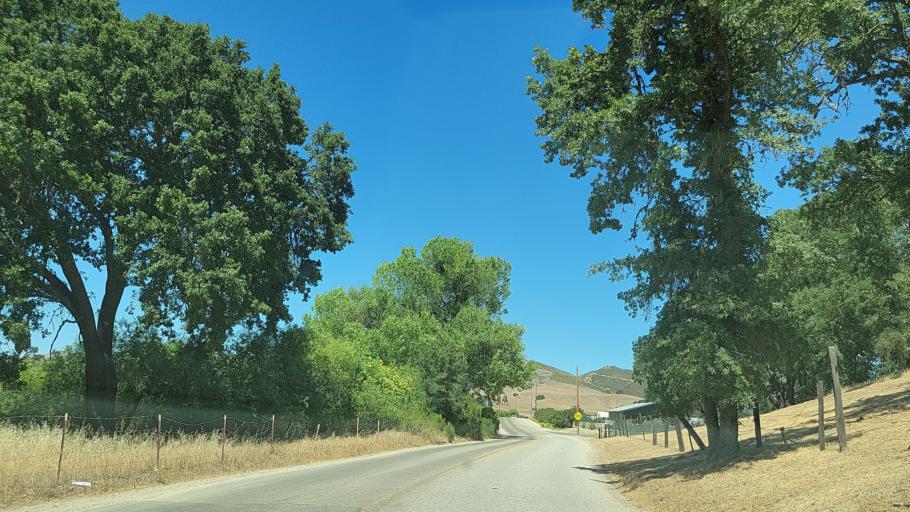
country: US
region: California
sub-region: San Luis Obispo County
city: Atascadero
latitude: 35.4587
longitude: -120.6290
